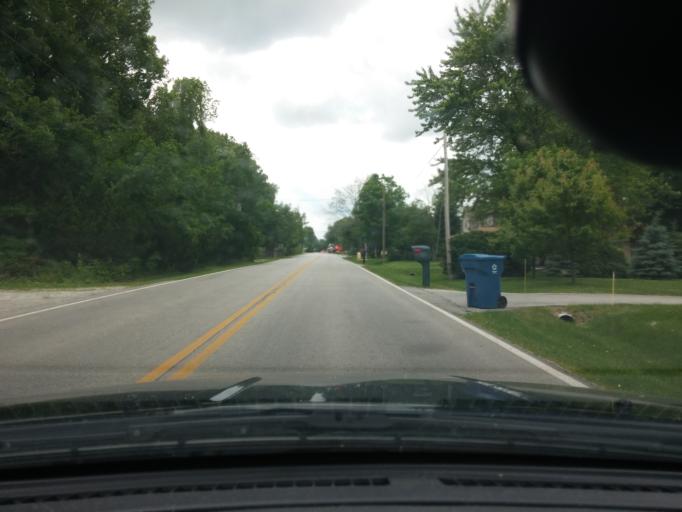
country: US
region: Indiana
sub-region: Tippecanoe County
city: West Lafayette
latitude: 40.4619
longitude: -86.9007
